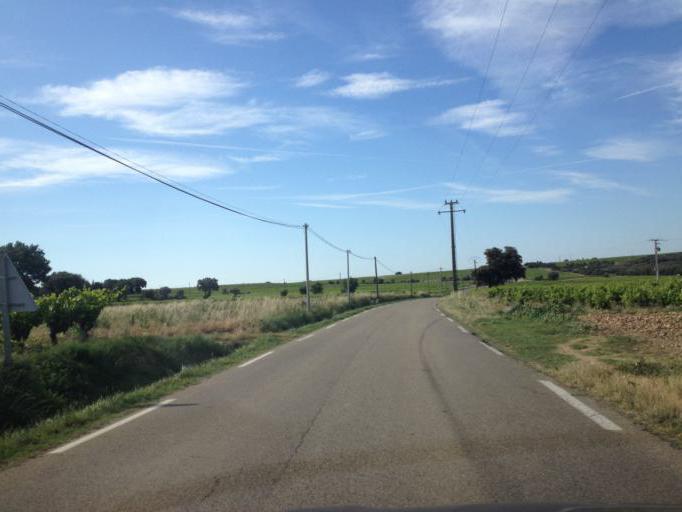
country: FR
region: Provence-Alpes-Cote d'Azur
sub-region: Departement du Vaucluse
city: Chateauneuf-du-Pape
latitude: 44.0799
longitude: 4.8315
